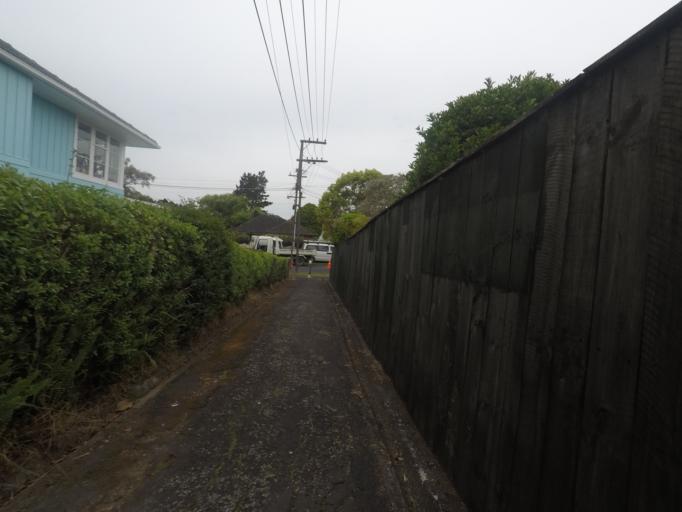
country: NZ
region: Auckland
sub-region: Auckland
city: Rosebank
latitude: -36.8756
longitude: 174.7140
